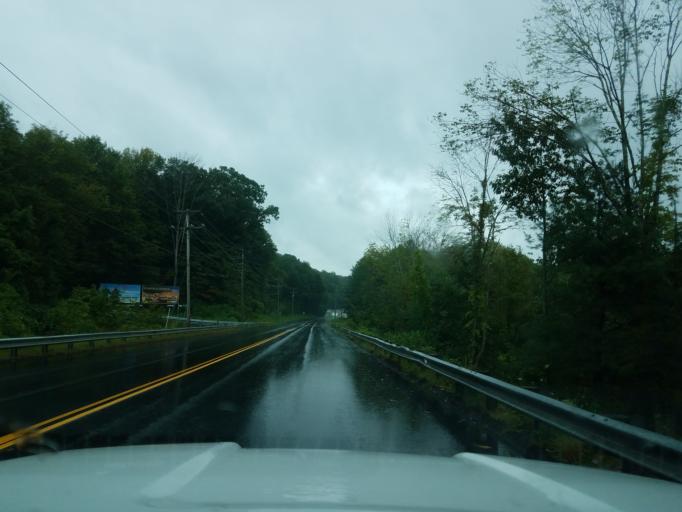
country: US
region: Connecticut
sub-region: Litchfield County
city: Winsted
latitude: 41.9121
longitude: -73.0225
